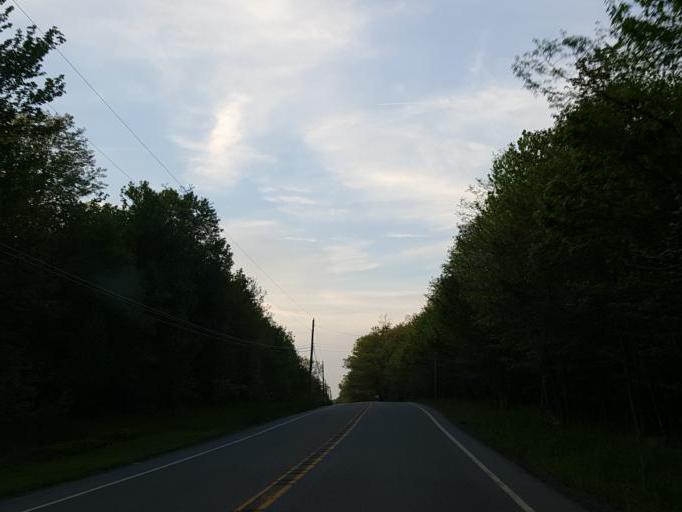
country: US
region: Pennsylvania
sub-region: Cambria County
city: Gallitzin
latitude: 40.4994
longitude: -78.5409
